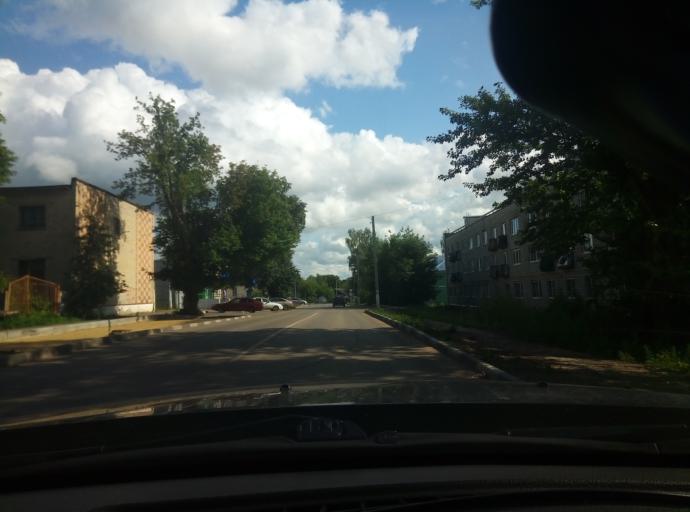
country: RU
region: Tula
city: Donskoy
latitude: 53.9696
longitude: 38.3316
